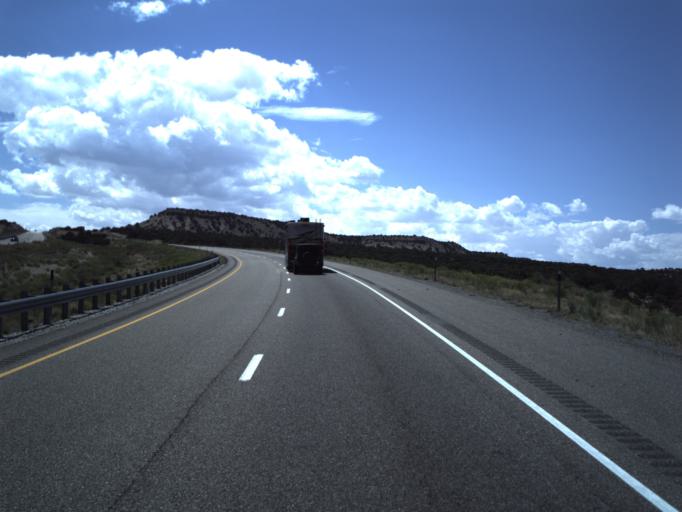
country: US
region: Utah
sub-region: Emery County
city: Castle Dale
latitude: 38.9145
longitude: -110.5195
